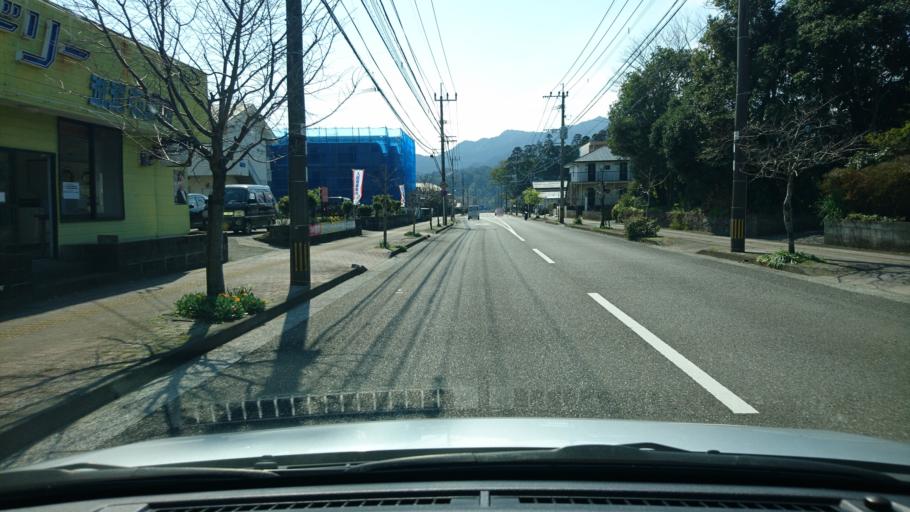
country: JP
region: Miyazaki
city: Miyazaki-shi
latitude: 31.8288
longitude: 131.4201
